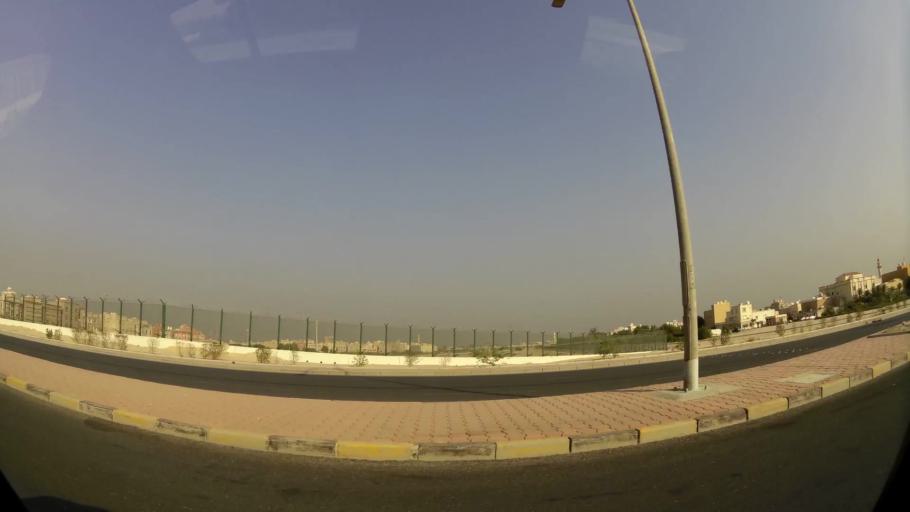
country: KW
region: Al Ahmadi
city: Ar Riqqah
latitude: 29.1200
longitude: 48.1049
